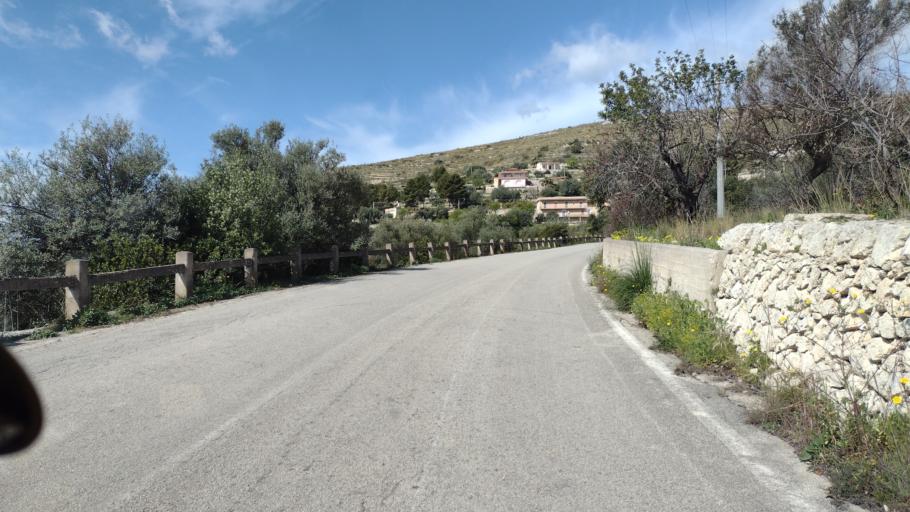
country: IT
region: Sicily
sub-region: Provincia di Siracusa
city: Noto
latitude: 36.9071
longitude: 15.0287
